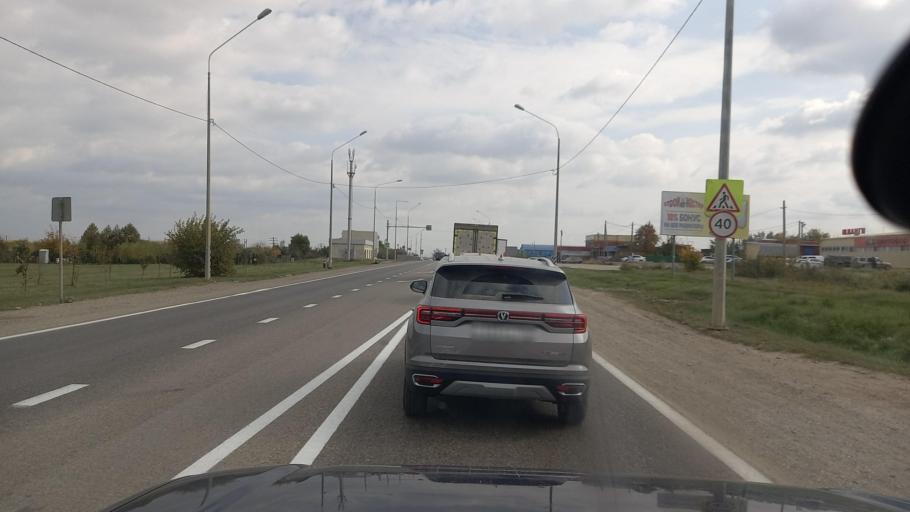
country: RU
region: Krasnodarskiy
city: Il'skiy
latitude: 44.8461
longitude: 38.5519
